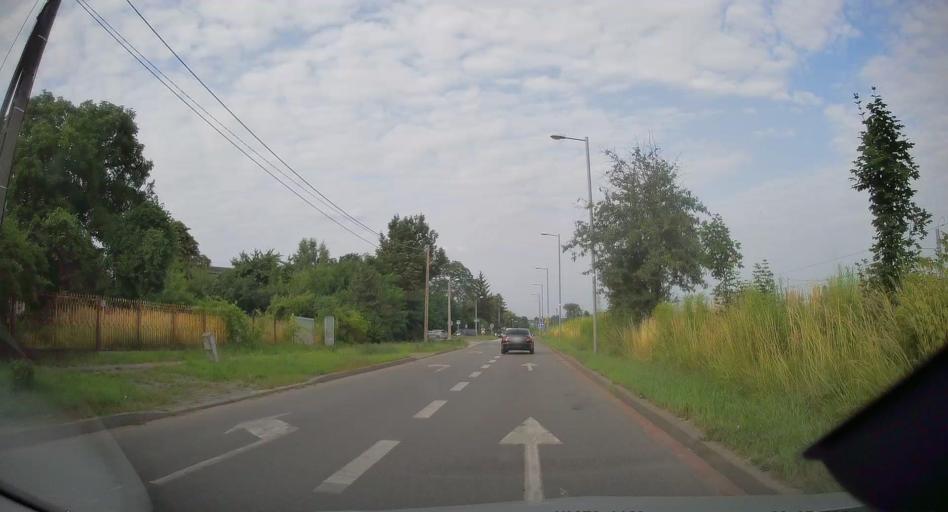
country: PL
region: Silesian Voivodeship
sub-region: Czestochowa
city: Czestochowa
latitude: 50.8282
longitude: 19.1362
